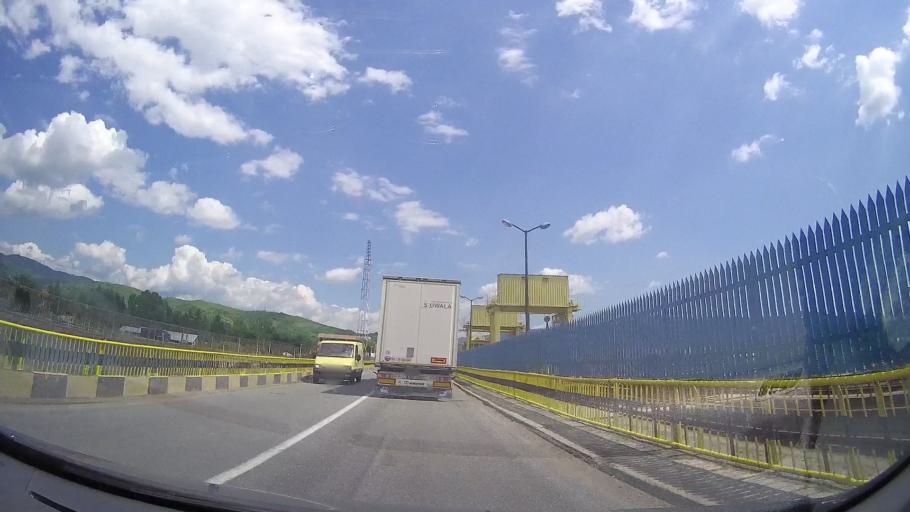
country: RO
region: Valcea
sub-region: Oras Calimanesti
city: Jiblea Veche
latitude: 45.2404
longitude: 24.3459
